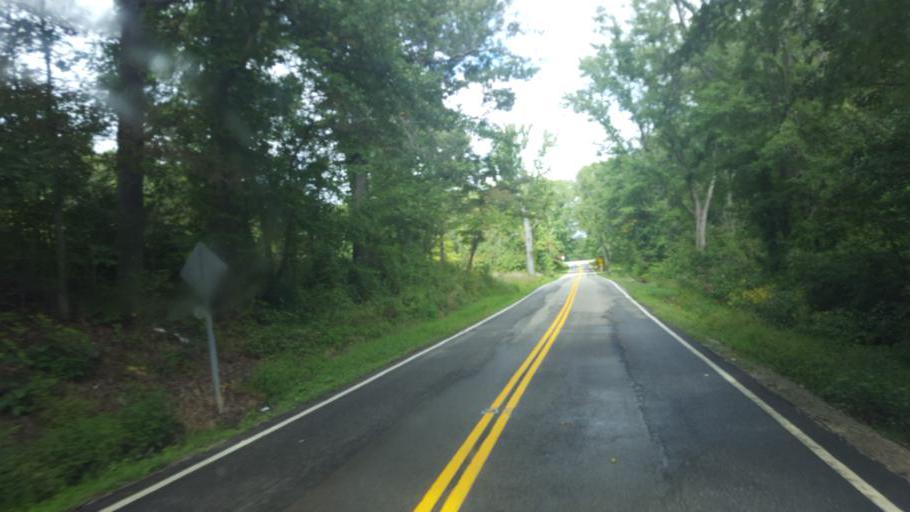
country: US
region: Ohio
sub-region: Jackson County
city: Oak Hill
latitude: 38.8880
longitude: -82.6625
